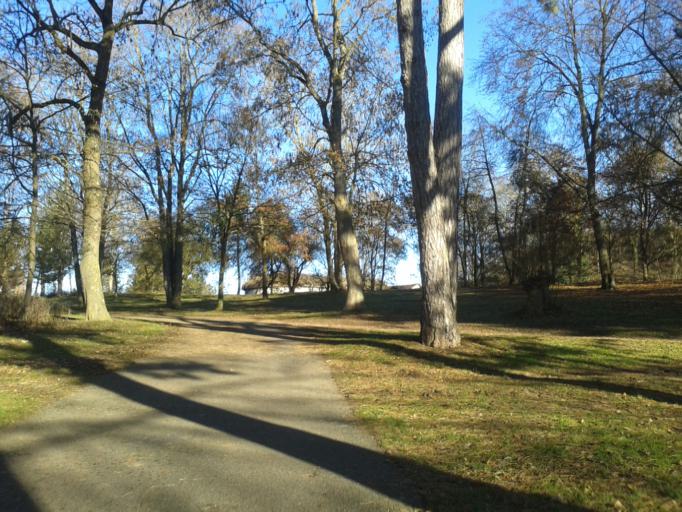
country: DE
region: Baden-Wuerttemberg
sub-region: Tuebingen Region
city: Ulm
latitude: 48.4102
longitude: 9.9617
